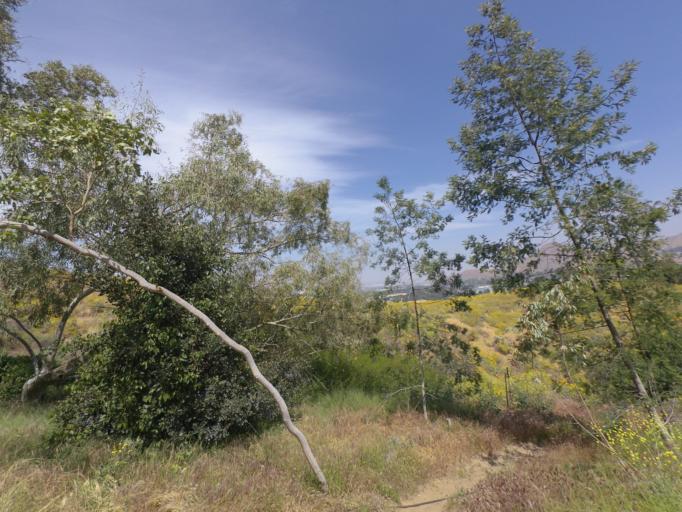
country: US
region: California
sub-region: Riverside County
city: Highgrove
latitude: 33.9677
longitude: -117.3205
